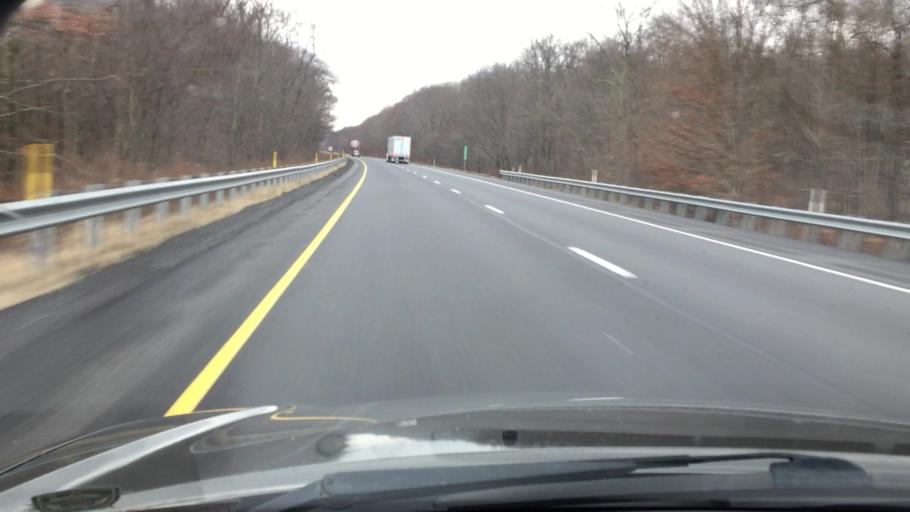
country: US
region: Pennsylvania
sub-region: Luzerne County
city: Freeland
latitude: 41.0613
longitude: -75.8999
